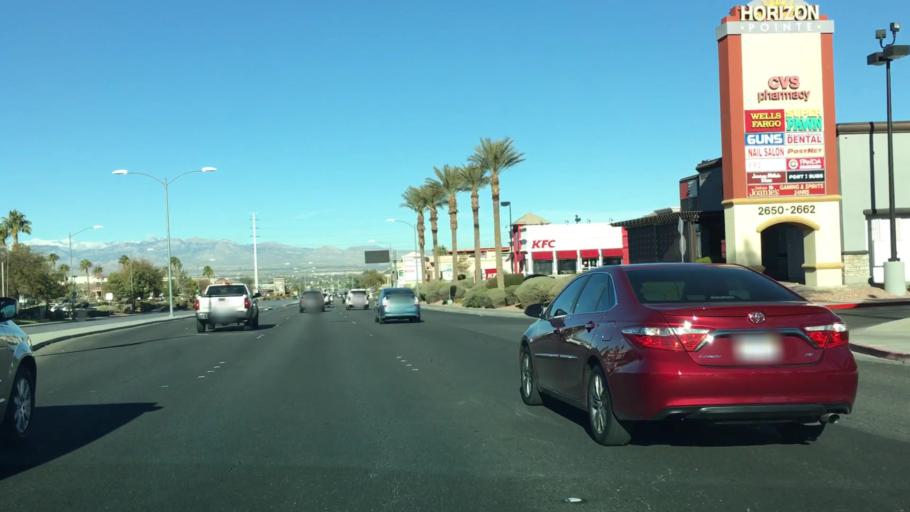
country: US
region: Nevada
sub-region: Clark County
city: Whitney
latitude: 36.0000
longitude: -115.1056
